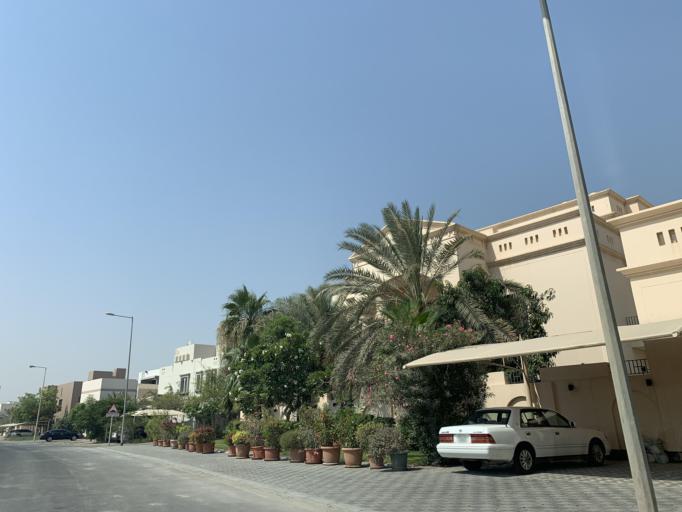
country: BH
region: Manama
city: Jidd Hafs
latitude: 26.1991
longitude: 50.5128
